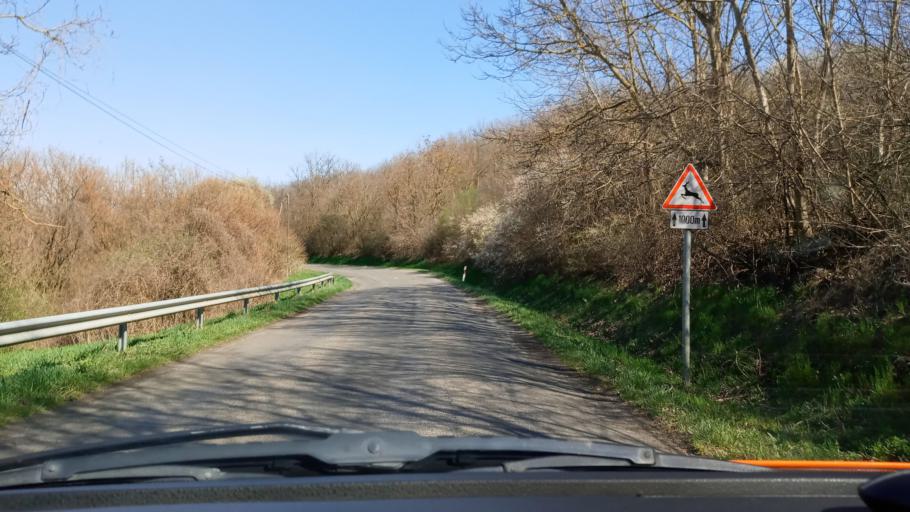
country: HU
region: Baranya
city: Boly
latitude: 46.0409
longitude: 18.4539
